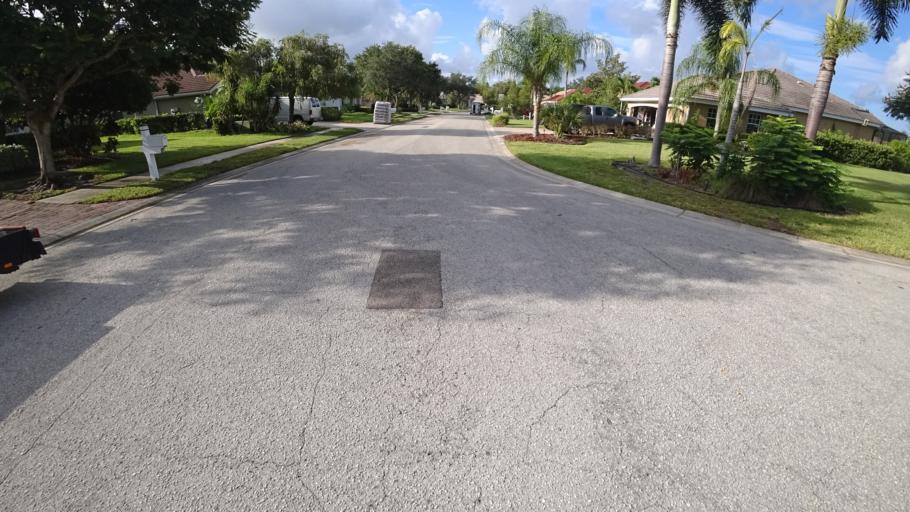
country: US
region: Florida
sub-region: Sarasota County
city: Desoto Lakes
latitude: 27.4228
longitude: -82.4814
